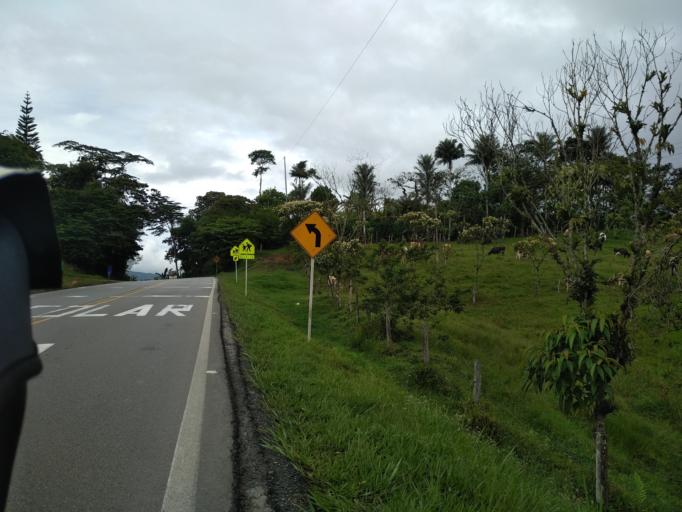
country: CO
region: Santander
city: Suaita
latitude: 6.1339
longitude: -73.3599
